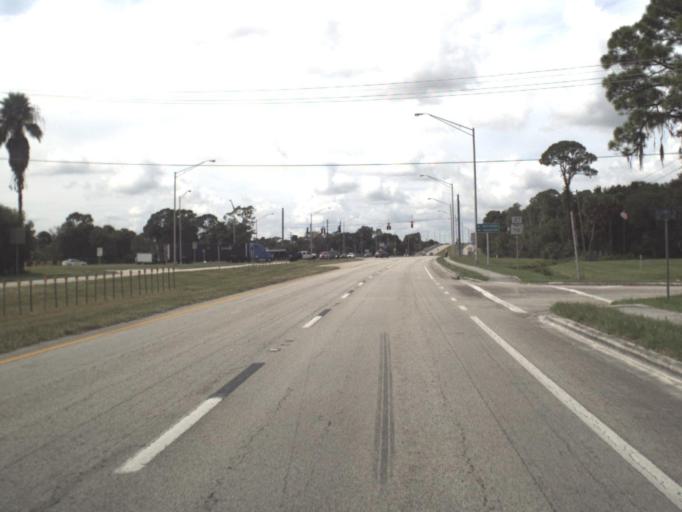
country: US
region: Florida
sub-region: Okeechobee County
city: Cypress Quarters
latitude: 27.2479
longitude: -80.7995
